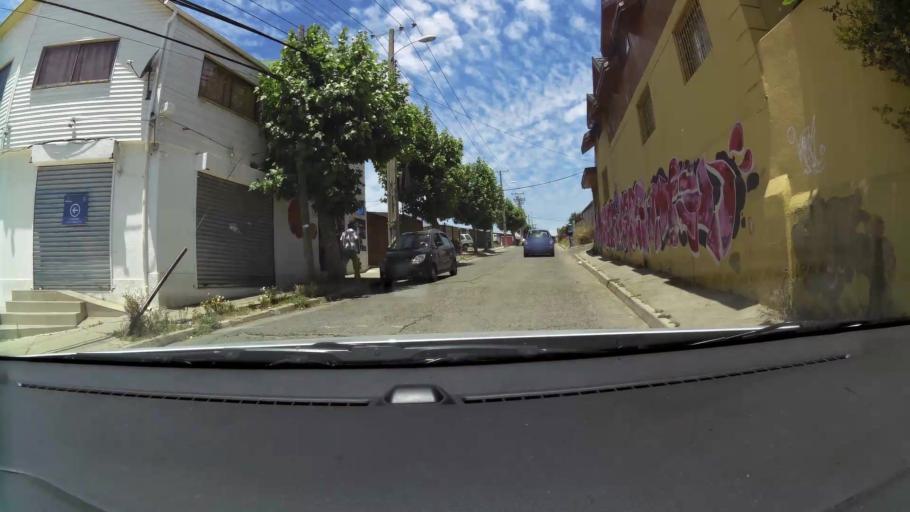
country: CL
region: Valparaiso
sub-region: Provincia de Valparaiso
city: Vina del Mar
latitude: -33.0461
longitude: -71.5789
